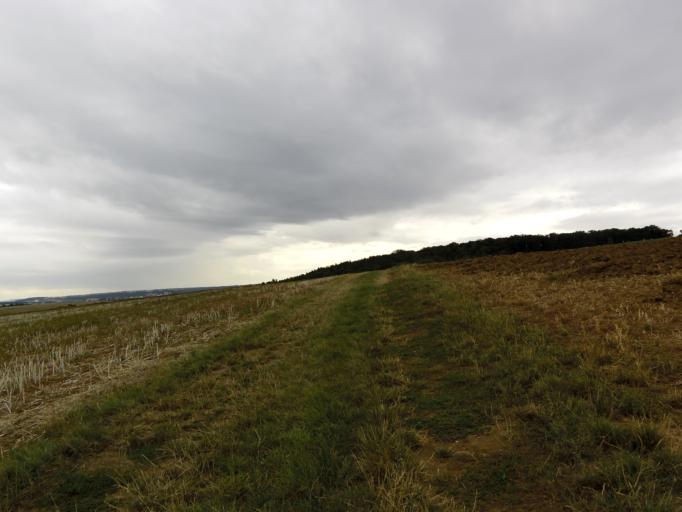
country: DE
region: Bavaria
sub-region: Regierungsbezirk Unterfranken
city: Rimpar
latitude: 49.8404
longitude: 9.9505
